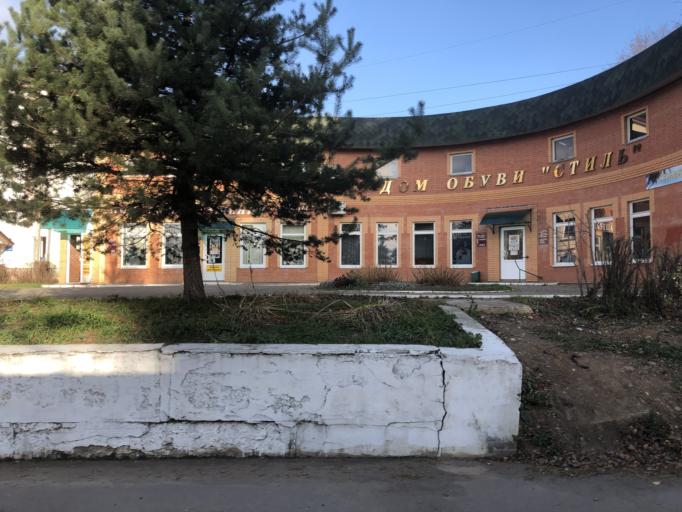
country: RU
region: Tverskaya
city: Rzhev
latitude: 56.2628
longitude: 34.3298
